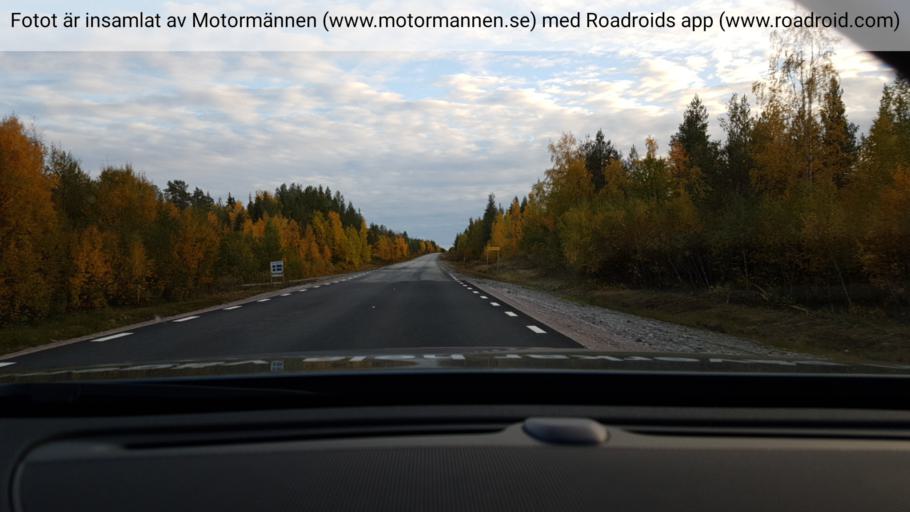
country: SE
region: Norrbotten
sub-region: Jokkmokks Kommun
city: Jokkmokk
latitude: 66.4463
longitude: 19.6937
